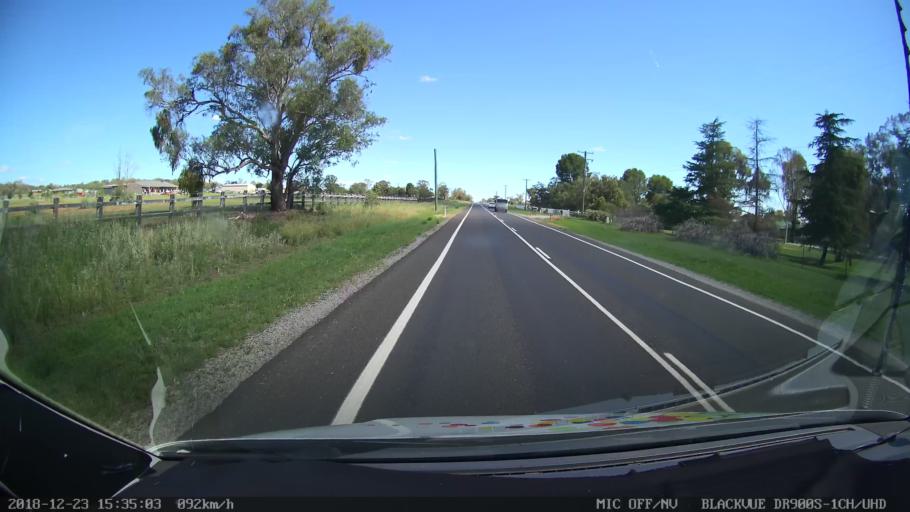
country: AU
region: New South Wales
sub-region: Tamworth Municipality
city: Tamworth
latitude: -31.0220
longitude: 150.8809
